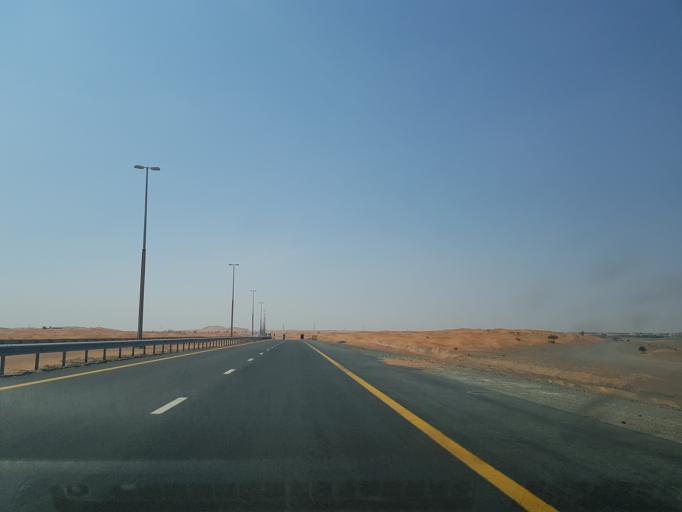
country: AE
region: Ash Shariqah
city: Adh Dhayd
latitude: 25.2396
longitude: 55.8872
